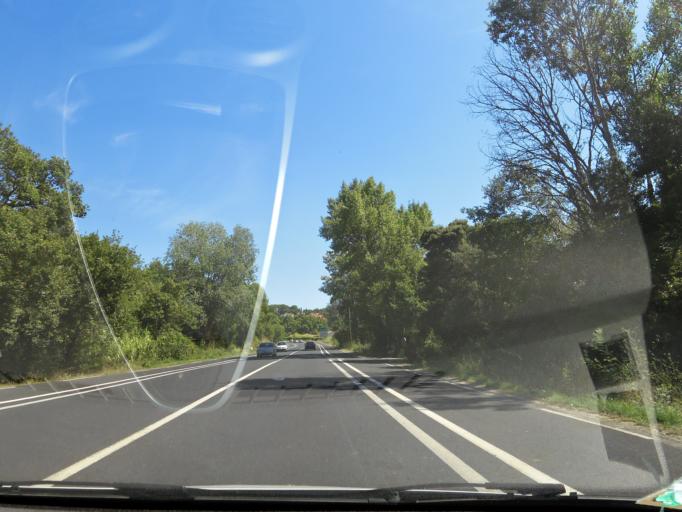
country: FR
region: Languedoc-Roussillon
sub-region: Departement de l'Herault
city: Clapiers
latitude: 43.6458
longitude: 3.8897
